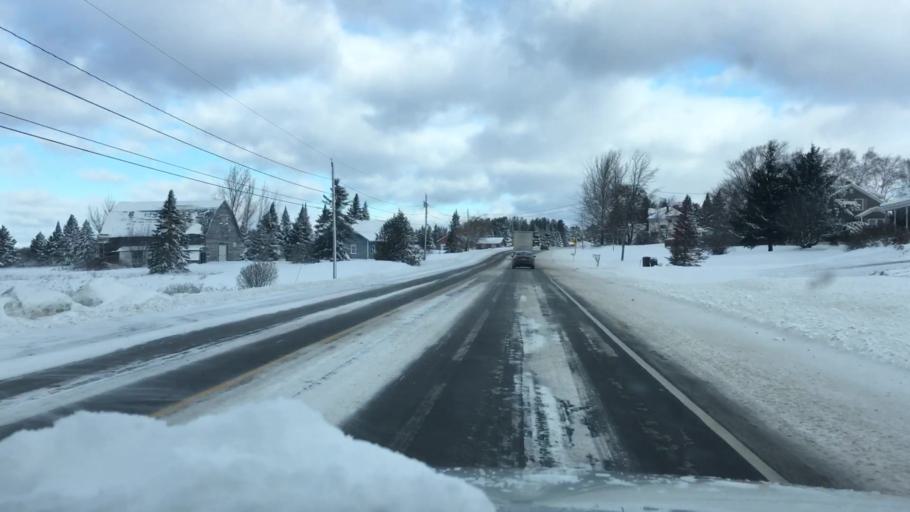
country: US
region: Maine
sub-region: Aroostook County
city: Caribou
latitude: 46.7890
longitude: -67.9903
